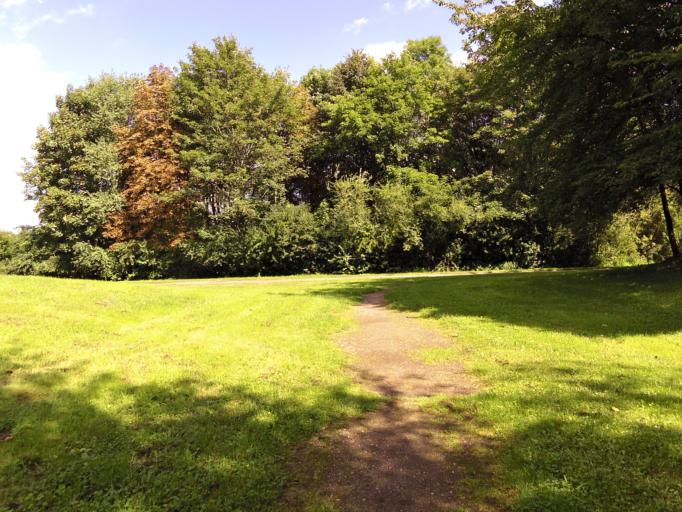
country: DE
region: Saxony
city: Markkleeberg
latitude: 51.2948
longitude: 12.4059
